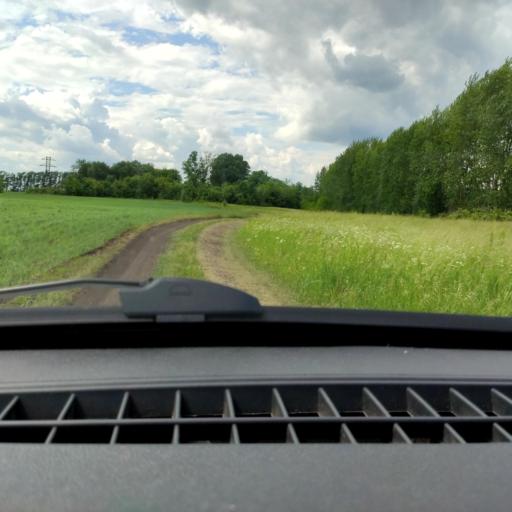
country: RU
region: Bashkortostan
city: Kabakovo
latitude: 54.5175
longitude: 56.0903
